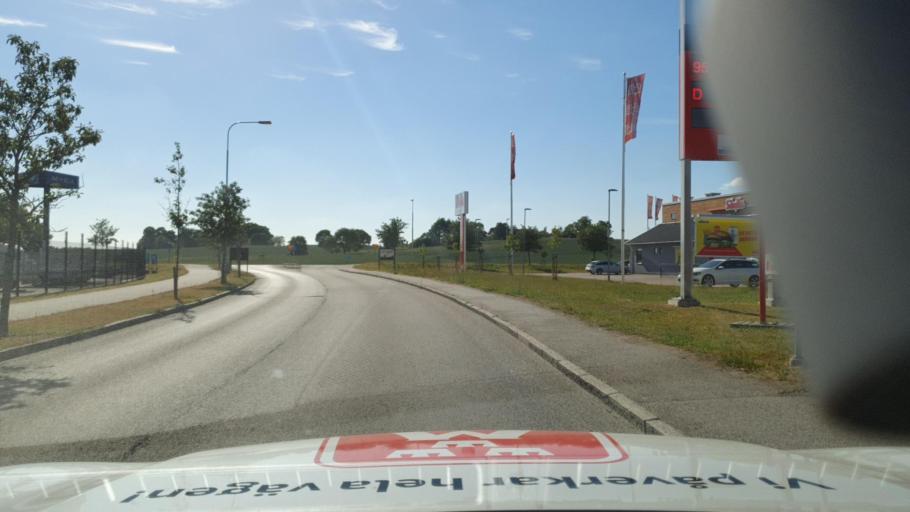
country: SE
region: Skane
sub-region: Skurups Kommun
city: Skurup
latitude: 55.4904
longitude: 13.4839
